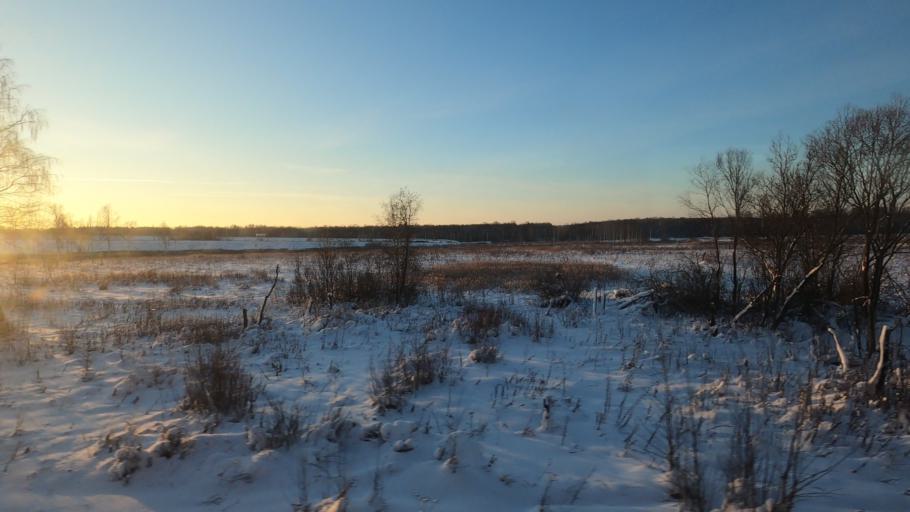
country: RU
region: Moskovskaya
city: Orud'yevo
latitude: 56.4133
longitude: 37.4966
